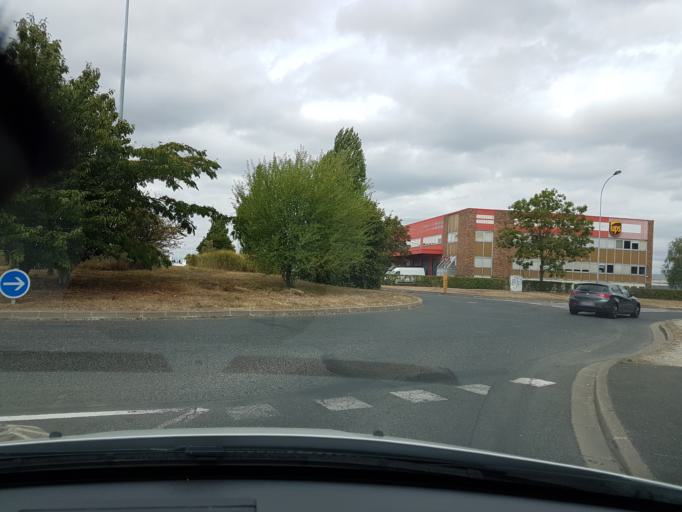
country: FR
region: Centre
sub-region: Departement d'Indre-et-Loire
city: Chambray-les-Tours
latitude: 47.3286
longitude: 0.7032
